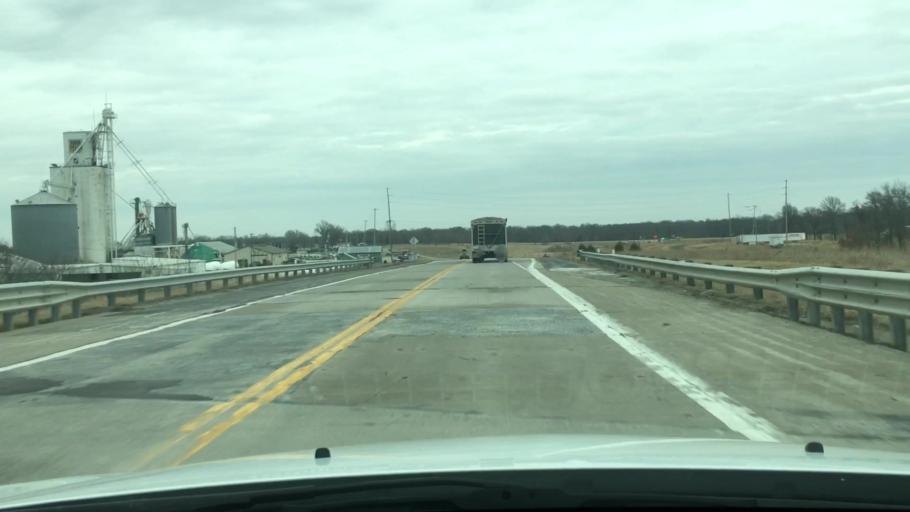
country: US
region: Missouri
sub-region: Audrain County
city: Mexico
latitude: 39.1575
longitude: -91.8429
